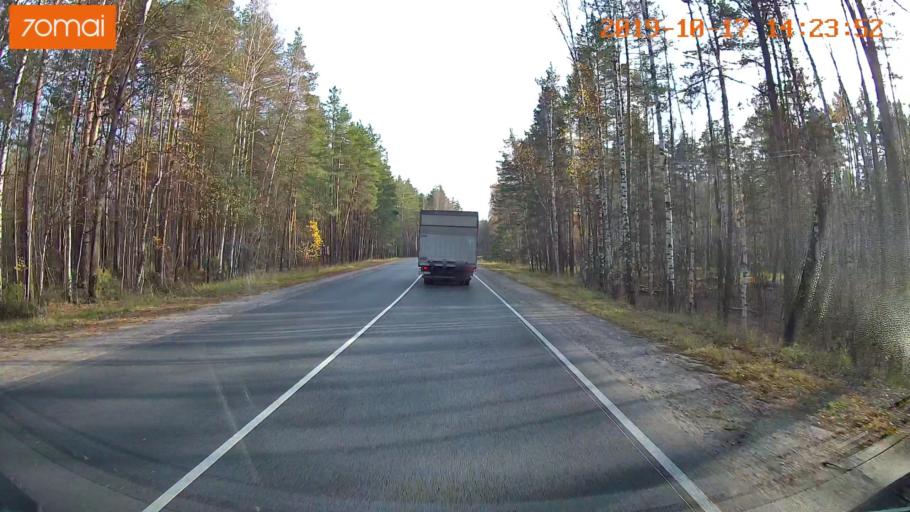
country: RU
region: Moskovskaya
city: Radovitskiy
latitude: 55.0143
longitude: 39.9630
